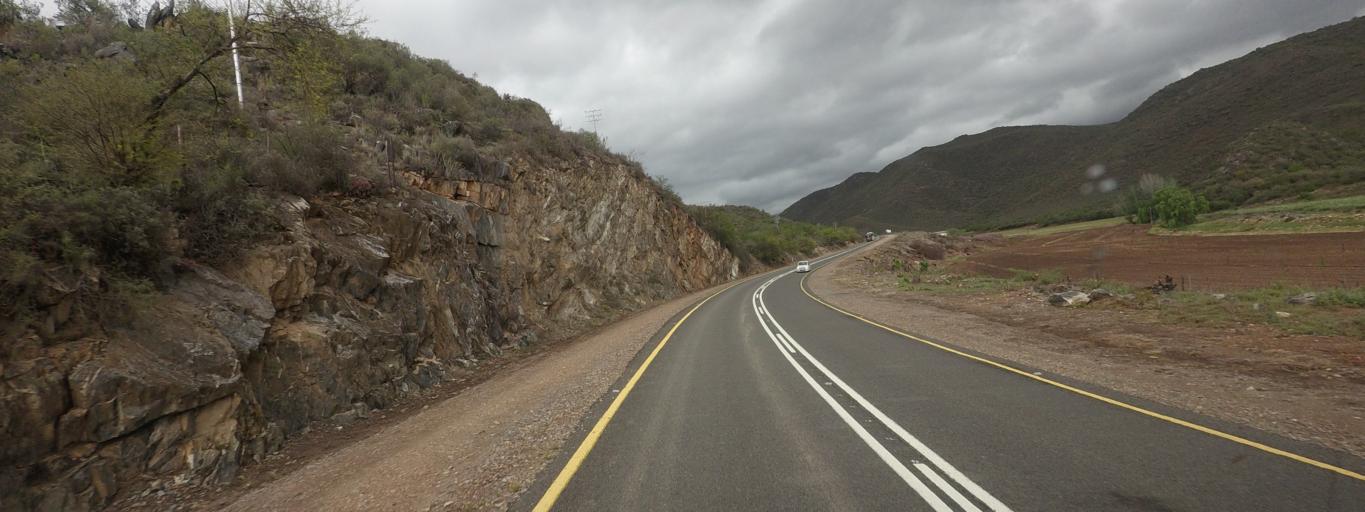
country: ZA
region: Western Cape
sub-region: Eden District Municipality
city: Oudtshoorn
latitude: -33.4101
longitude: 22.2316
